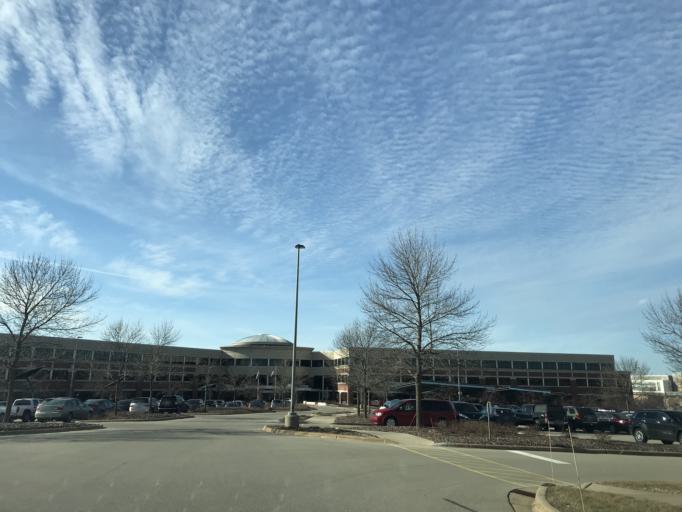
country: US
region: Wisconsin
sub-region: Dane County
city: Windsor
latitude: 43.1507
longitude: -89.2939
